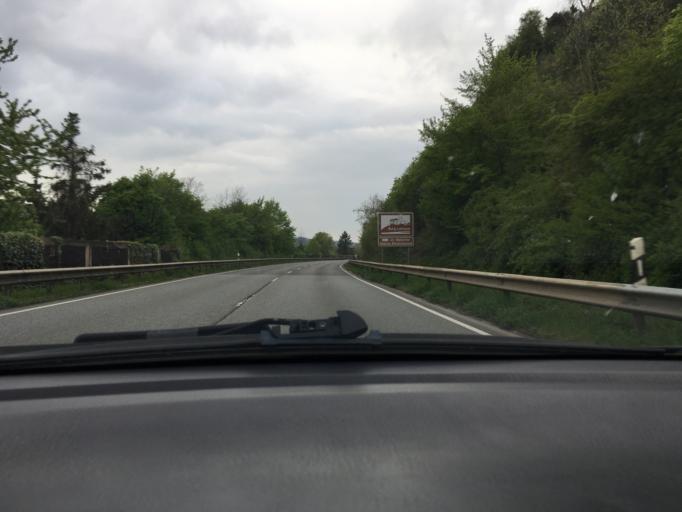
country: DE
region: Rheinland-Pfalz
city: Lahnstein
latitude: 50.2987
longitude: 7.6161
